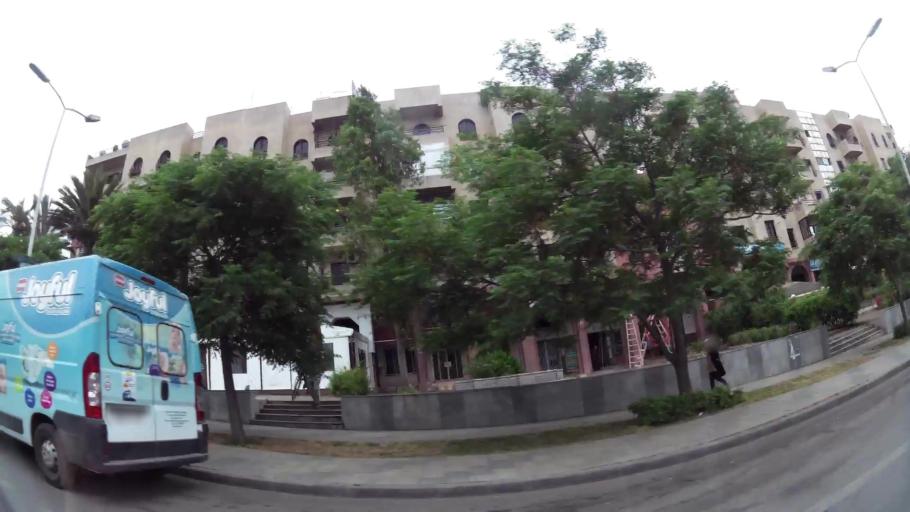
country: MA
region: Rabat-Sale-Zemmour-Zaer
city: Sale
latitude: 34.0347
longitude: -6.8012
